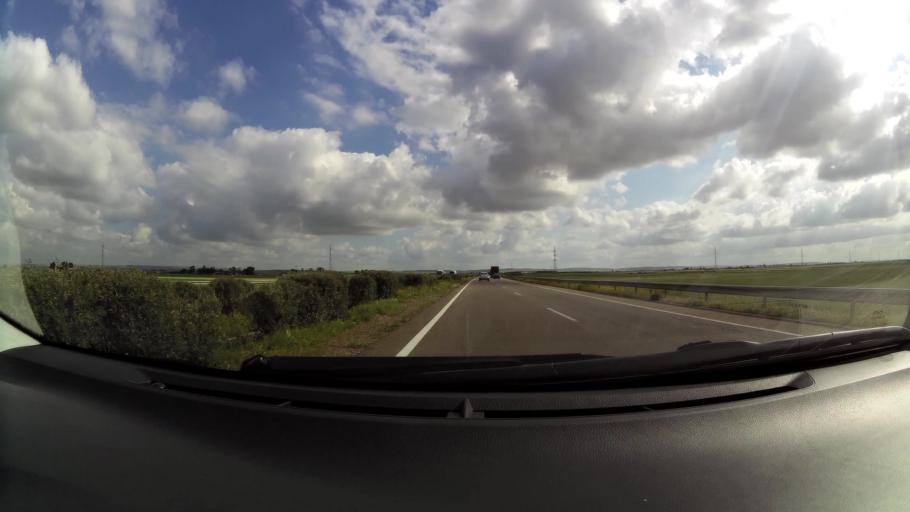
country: MA
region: Chaouia-Ouardigha
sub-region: Settat Province
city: Berrechid
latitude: 33.1604
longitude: -7.5705
